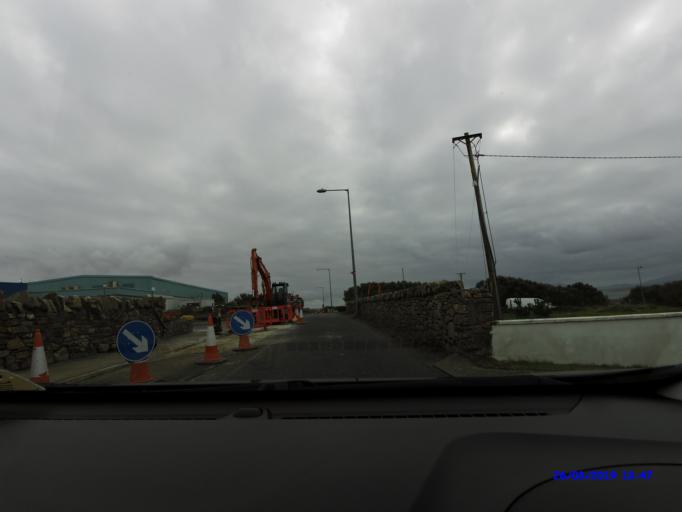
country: IE
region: Connaught
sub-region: Maigh Eo
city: Belmullet
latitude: 54.2203
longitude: -9.9861
